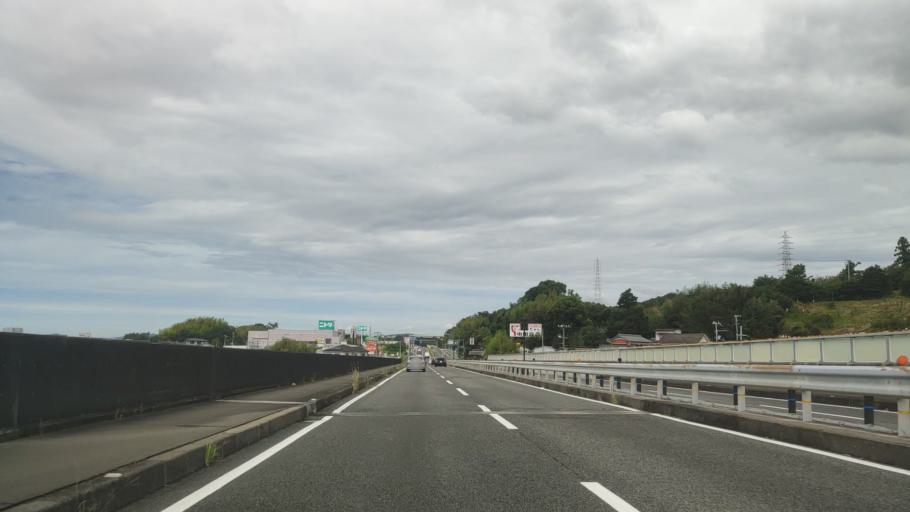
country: JP
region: Wakayama
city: Tanabe
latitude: 33.7187
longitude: 135.4069
